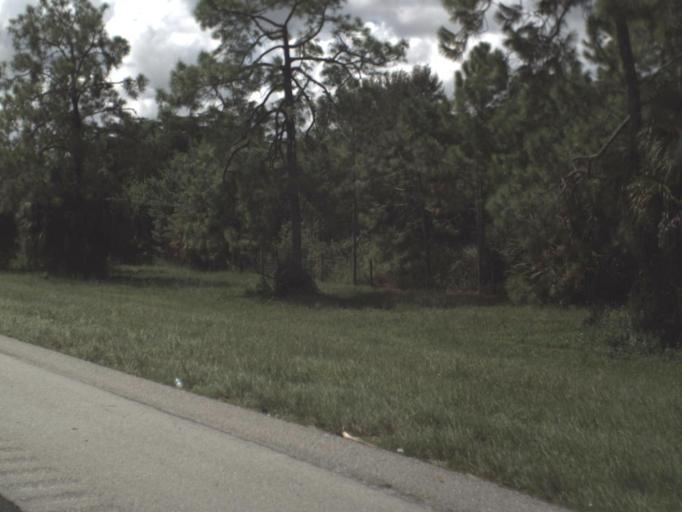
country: US
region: Florida
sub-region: Lee County
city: Bonita Springs
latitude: 26.3225
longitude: -81.7483
